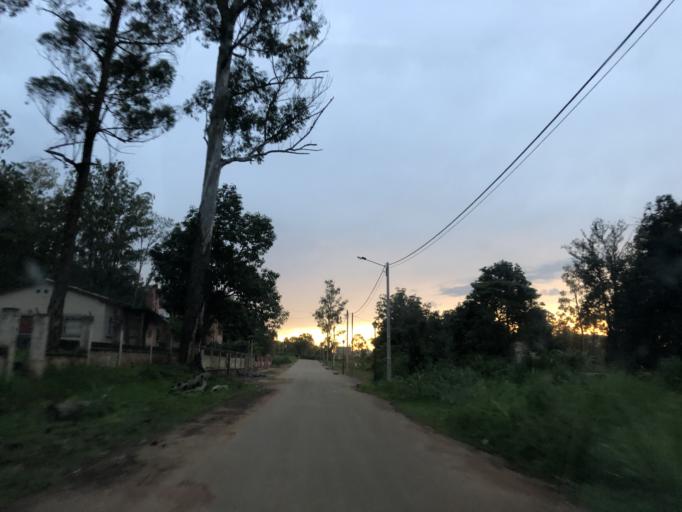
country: AO
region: Cuanza Sul
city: Uacu Cungo
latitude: -11.3689
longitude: 15.1190
